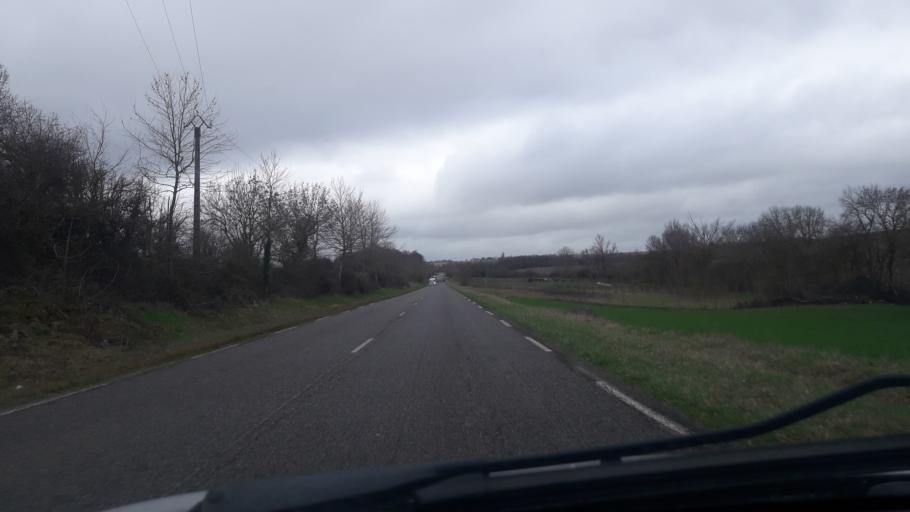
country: FR
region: Midi-Pyrenees
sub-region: Departement du Gers
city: Gimont
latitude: 43.6731
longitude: 1.0126
